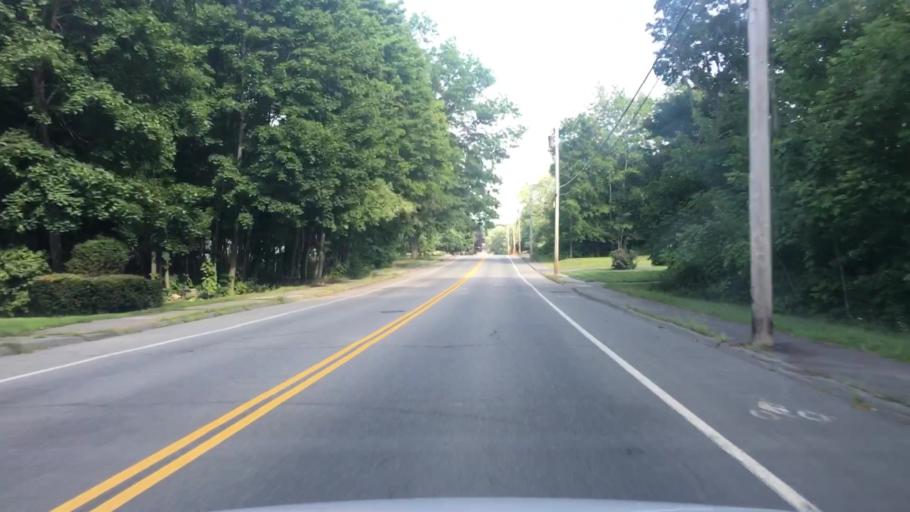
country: US
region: Maine
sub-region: Kennebec County
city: Waterville
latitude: 44.5559
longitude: -69.6524
